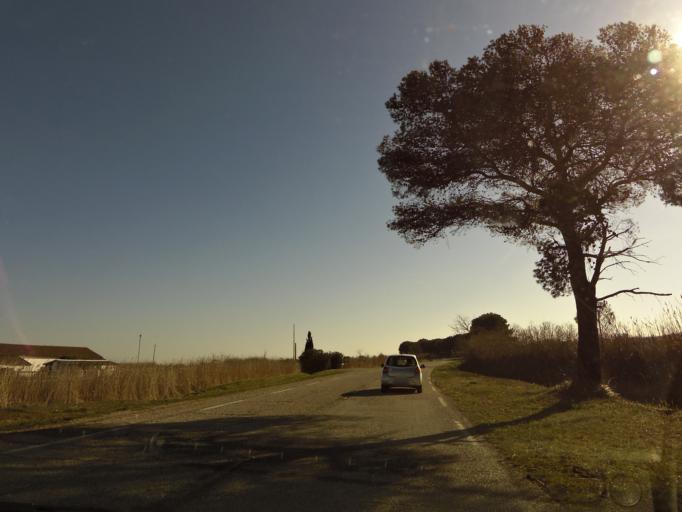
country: FR
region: Provence-Alpes-Cote d'Azur
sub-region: Departement des Bouches-du-Rhone
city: Saintes-Maries-de-la-Mer
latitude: 43.5070
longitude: 4.3775
